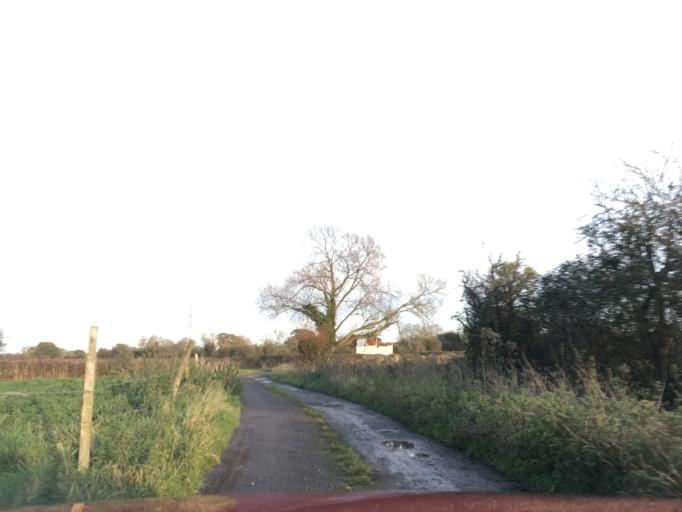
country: GB
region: England
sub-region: South Gloucestershire
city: Thornbury
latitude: 51.6316
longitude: -2.5314
